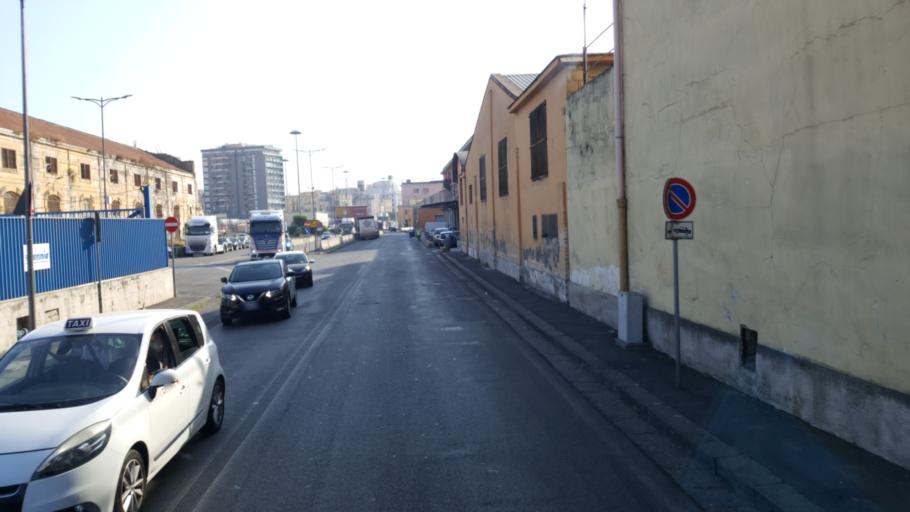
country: IT
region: Campania
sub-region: Provincia di Napoli
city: Napoli
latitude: 40.8430
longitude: 14.2593
